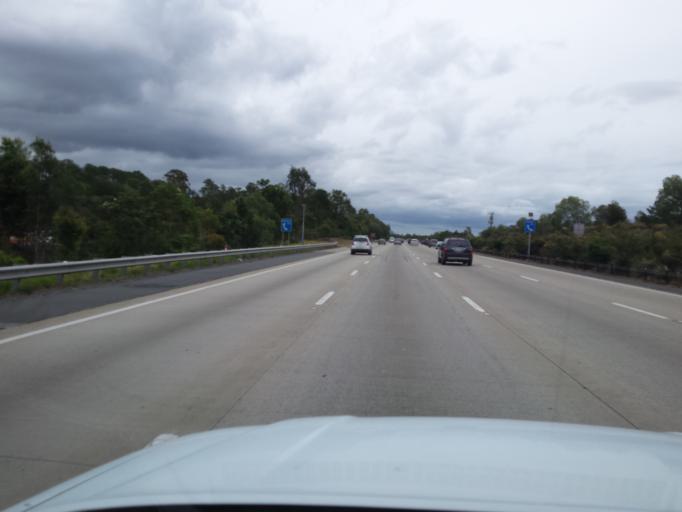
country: AU
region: Queensland
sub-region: Gold Coast
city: Nerang
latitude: -27.9394
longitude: 153.3368
